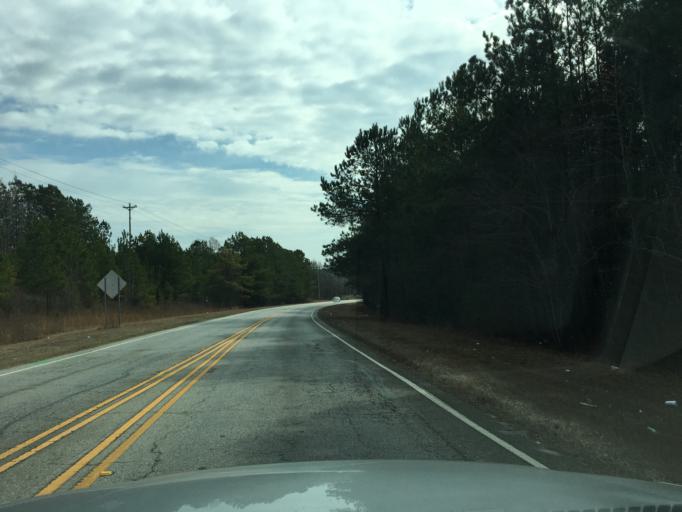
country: US
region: South Carolina
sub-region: Laurens County
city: Clinton
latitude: 34.4923
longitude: -81.8656
